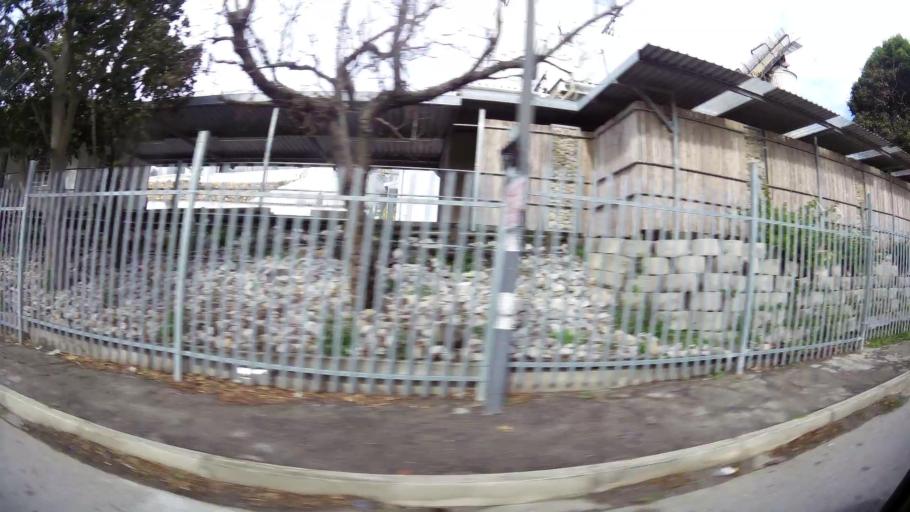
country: ZA
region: Eastern Cape
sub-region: Nelson Mandela Bay Metropolitan Municipality
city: Port Elizabeth
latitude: -33.9304
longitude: 25.5548
